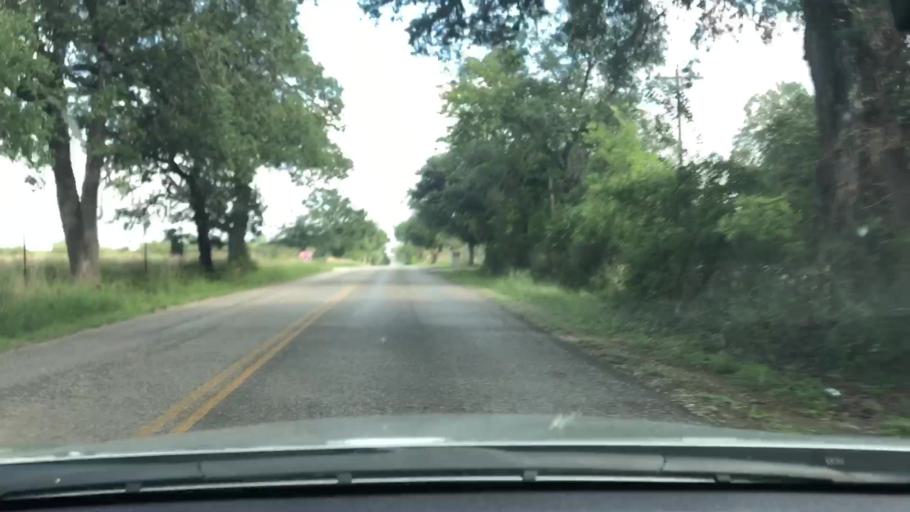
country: US
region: Texas
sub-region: Bexar County
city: Fair Oaks Ranch
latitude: 29.7864
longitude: -98.6713
